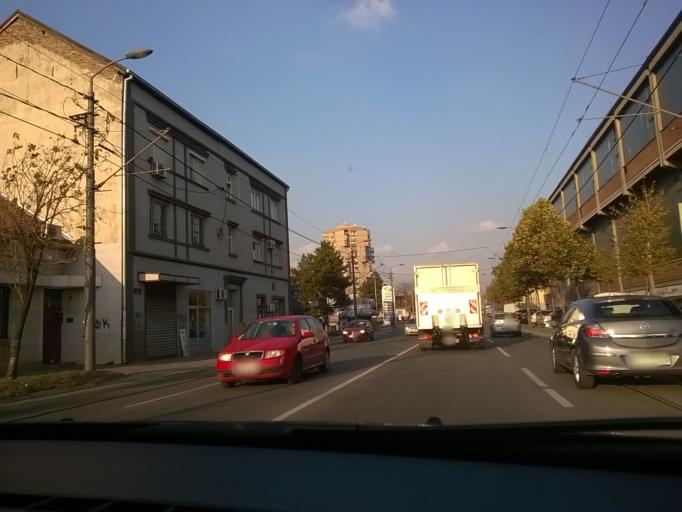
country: RS
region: Central Serbia
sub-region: Belgrade
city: Vracar
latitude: 44.8130
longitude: 20.4891
